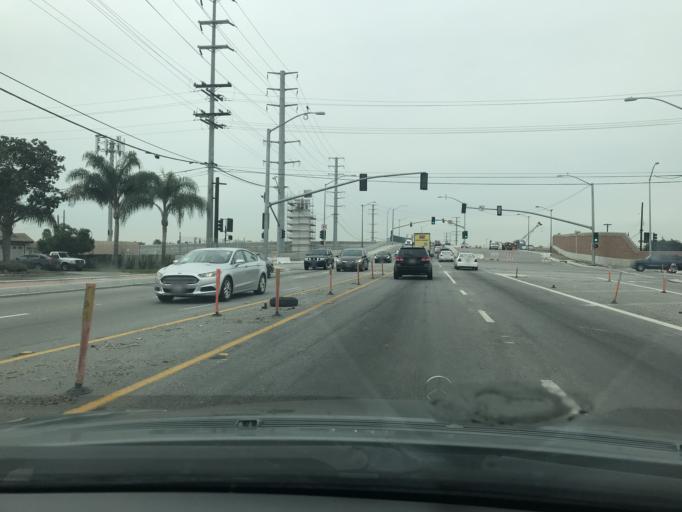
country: US
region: California
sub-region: Los Angeles County
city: Santa Fe Springs
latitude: 33.9353
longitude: -118.0899
